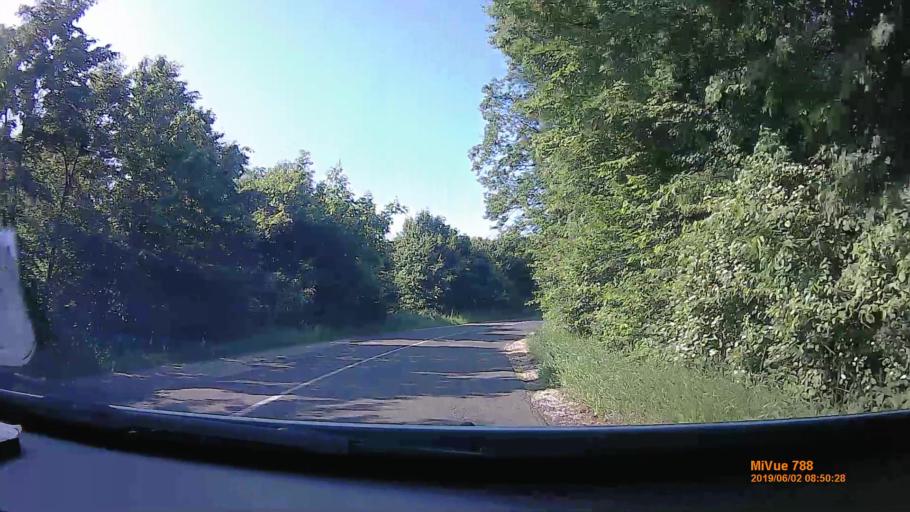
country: HU
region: Borsod-Abauj-Zemplen
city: Sajobabony
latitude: 48.1469
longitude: 20.6894
